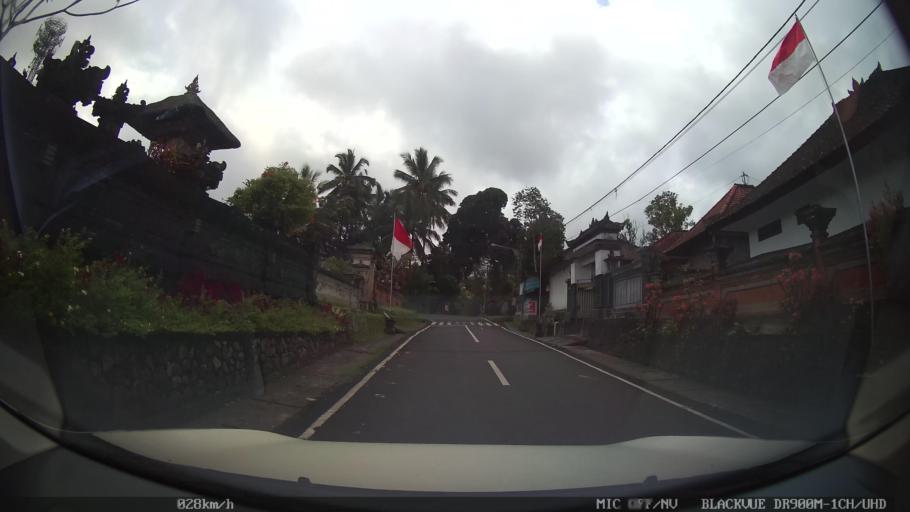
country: ID
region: Bali
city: Pemijian
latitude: -8.4435
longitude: 115.2261
